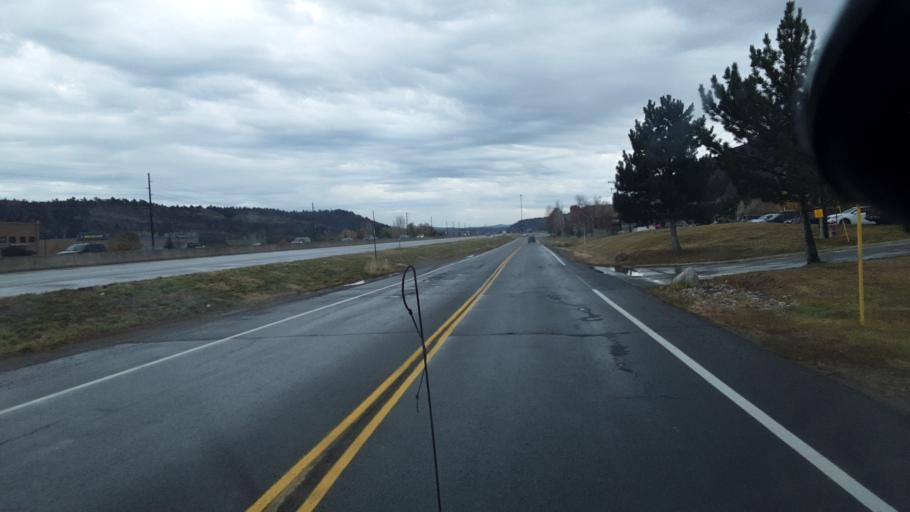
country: US
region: Colorado
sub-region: La Plata County
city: Durango
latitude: 37.2500
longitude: -107.8759
